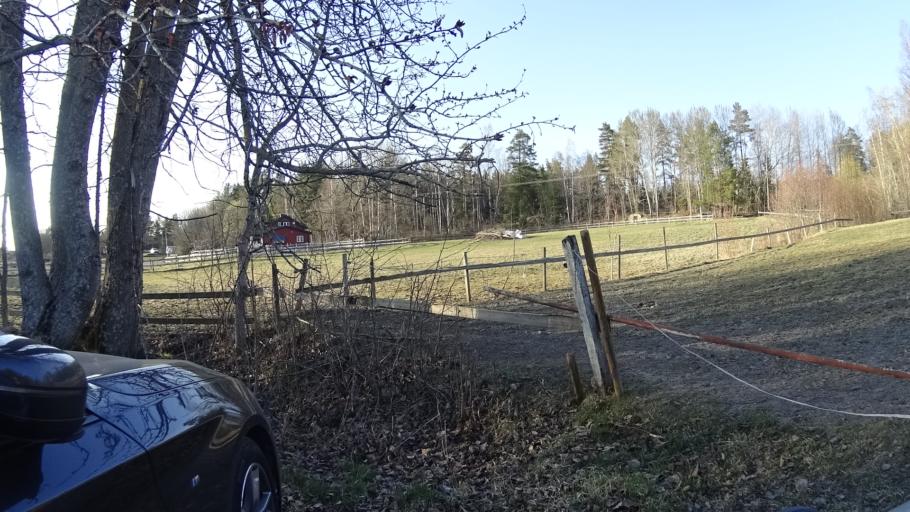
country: SE
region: Stockholm
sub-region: Osterakers Kommun
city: Akersberga
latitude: 59.4516
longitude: 18.2301
